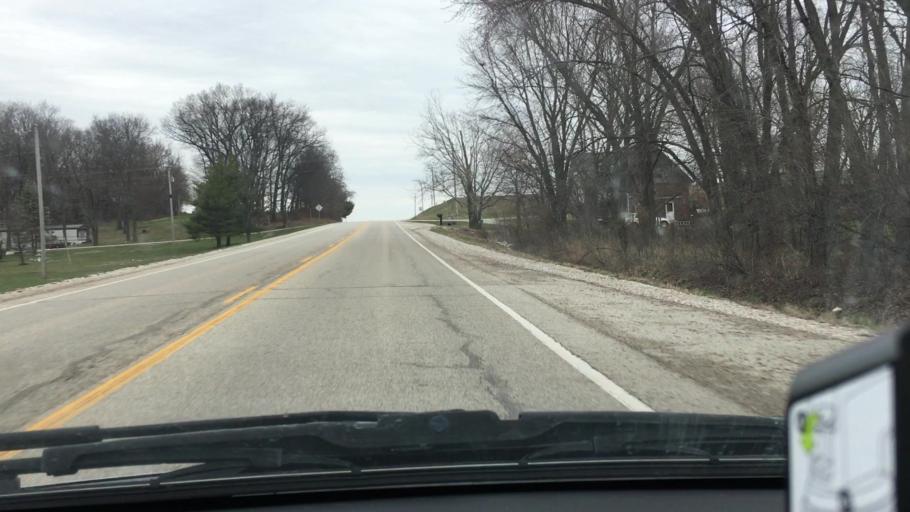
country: US
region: Indiana
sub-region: Greene County
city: Bloomfield
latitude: 38.9932
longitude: -87.0163
